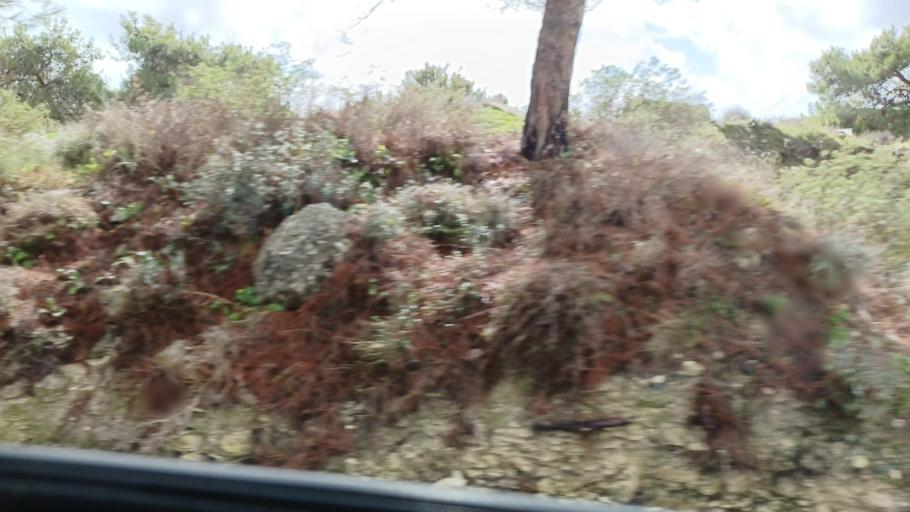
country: CY
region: Limassol
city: Sotira
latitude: 34.7110
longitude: 32.8647
